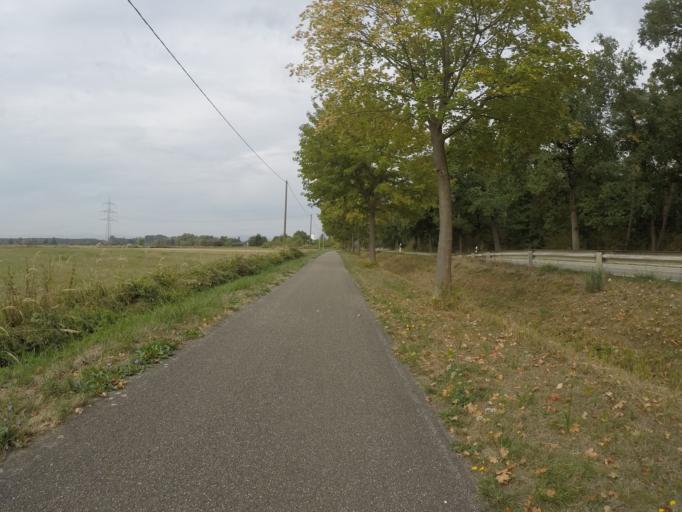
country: DE
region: Rheinland-Pfalz
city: Bohl-Iggelheim
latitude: 49.3570
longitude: 8.3280
